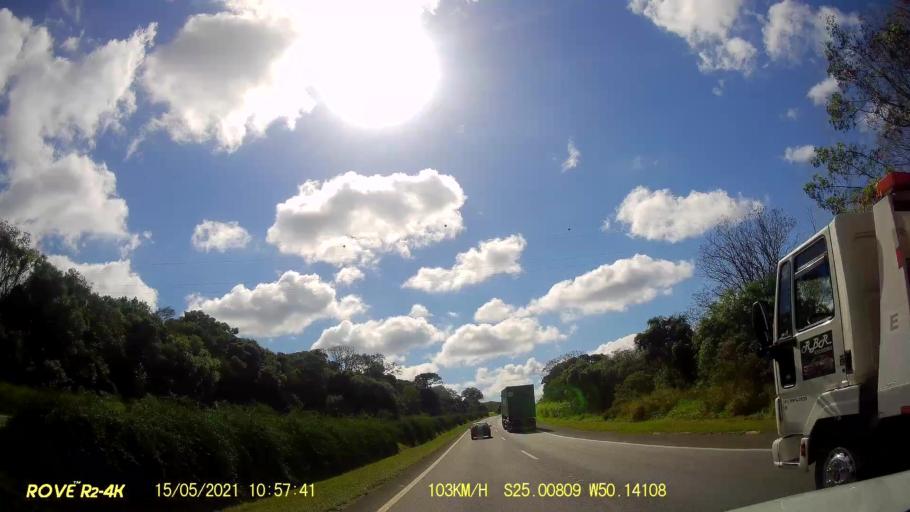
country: BR
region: Parana
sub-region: Carambei
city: Carambei
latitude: -25.0077
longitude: -50.1407
